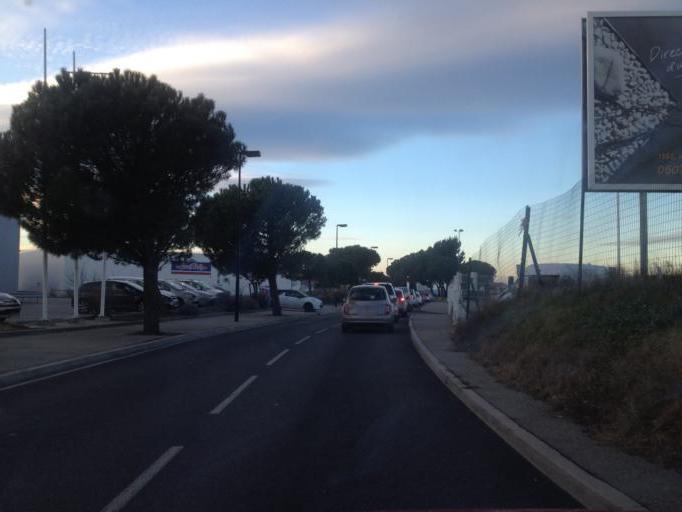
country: FR
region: Provence-Alpes-Cote d'Azur
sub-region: Departement du Vaucluse
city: Orange
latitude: 44.1176
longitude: 4.8414
